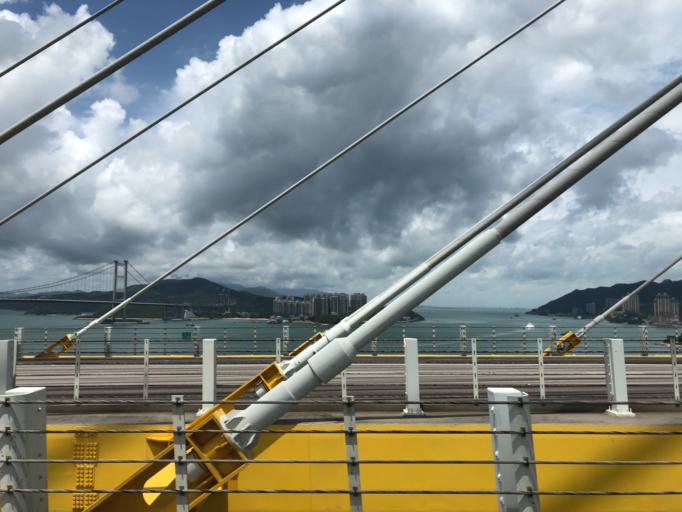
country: HK
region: Tsuen Wan
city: Tsuen Wan
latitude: 22.3631
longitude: 114.0803
